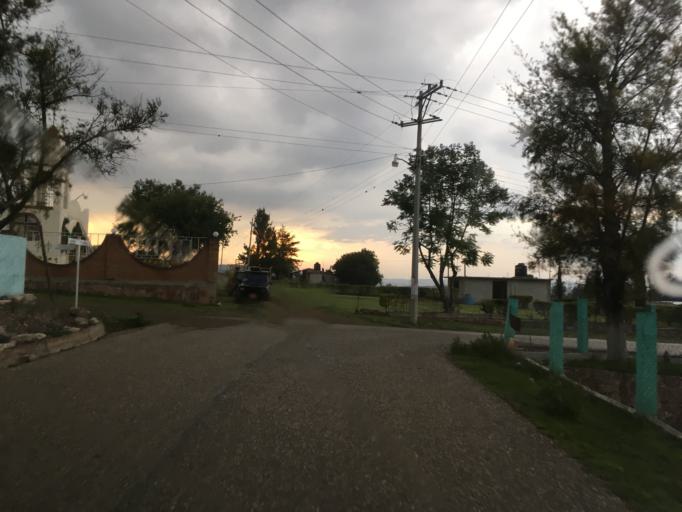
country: MX
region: Oaxaca
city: Santiago Tilantongo
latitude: 17.2890
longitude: -97.2837
